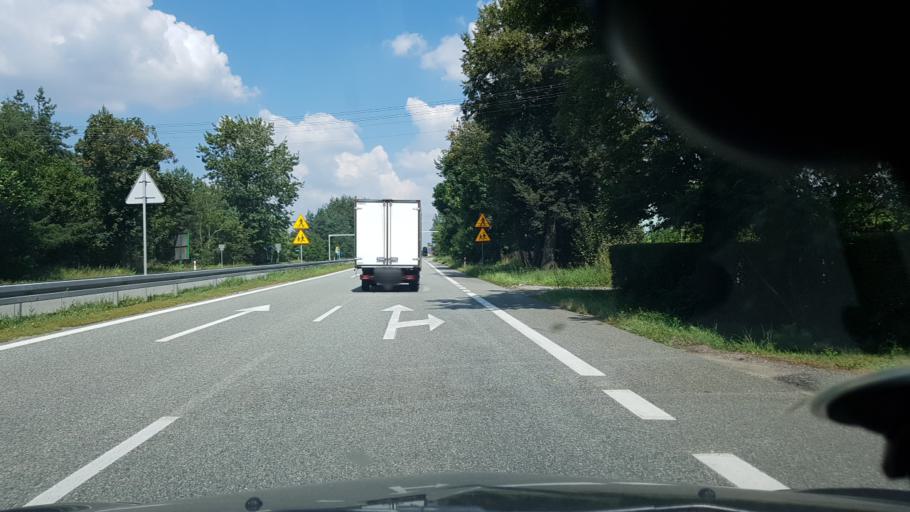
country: PL
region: Silesian Voivodeship
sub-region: Powiat pszczynski
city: Rudziczka
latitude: 50.0821
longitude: 18.7534
